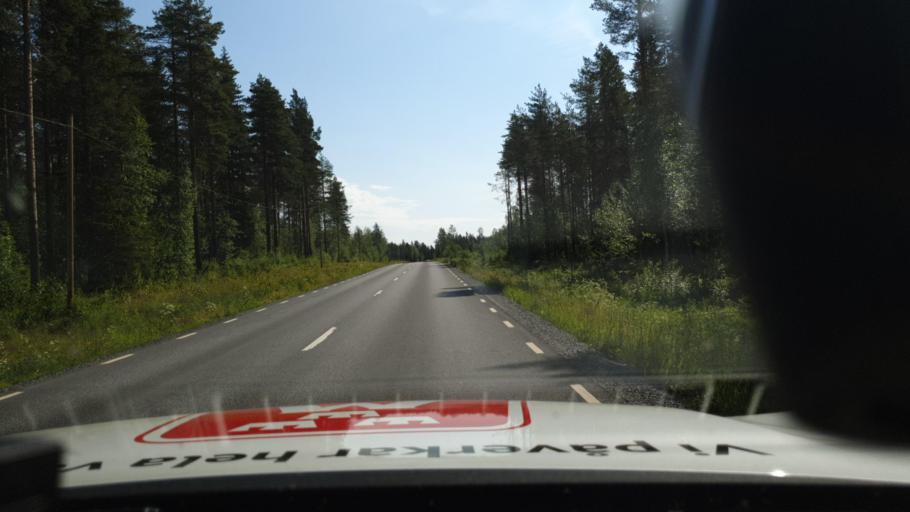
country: SE
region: Norrbotten
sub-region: Lulea Kommun
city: Ranea
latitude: 65.7905
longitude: 22.1340
